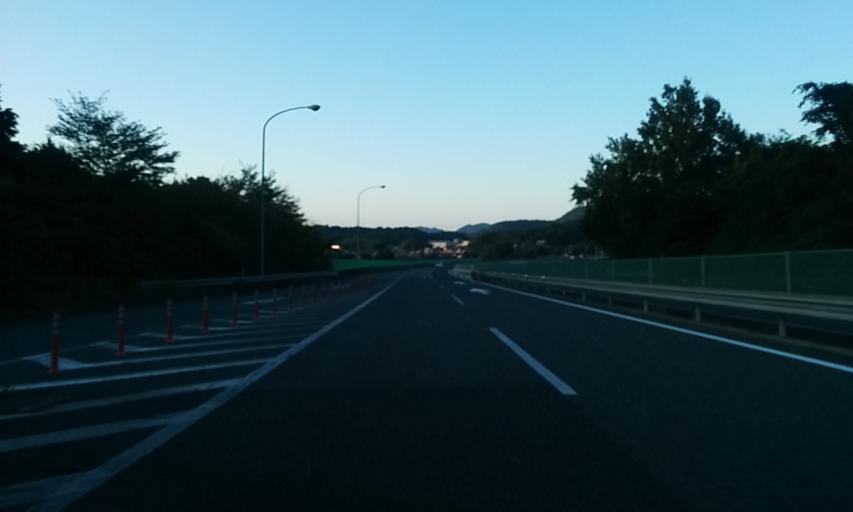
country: JP
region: Kyoto
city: Fukuchiyama
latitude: 35.2597
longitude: 135.1831
